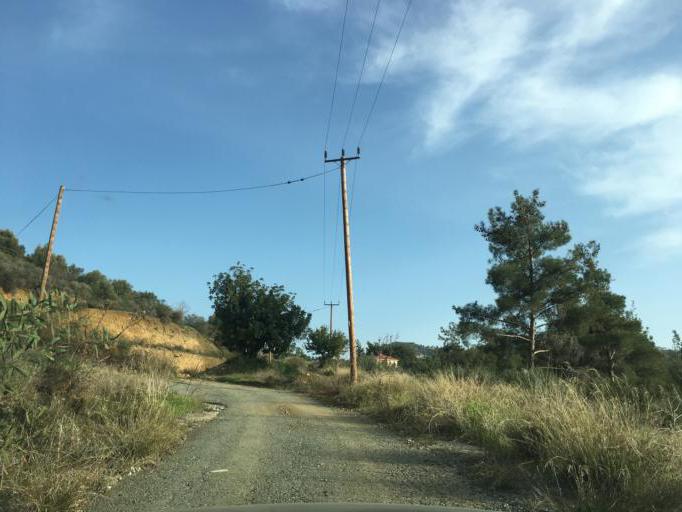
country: CY
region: Limassol
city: Pelendri
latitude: 34.8272
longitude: 32.9676
